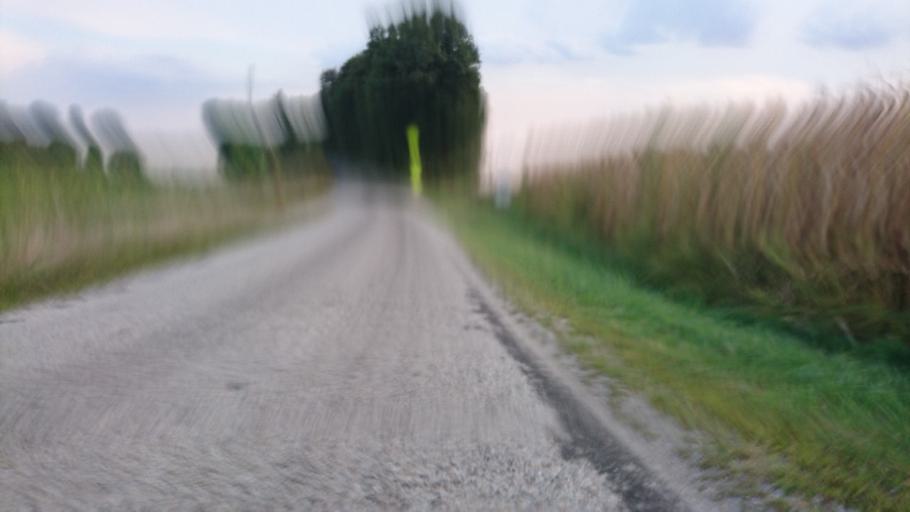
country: US
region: Illinois
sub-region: Logan County
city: Atlanta
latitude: 40.2311
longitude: -89.2048
